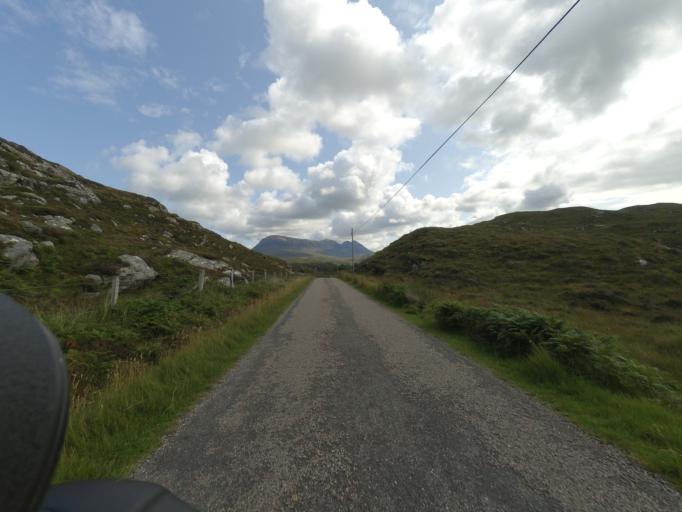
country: GB
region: Scotland
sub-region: Highland
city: Ullapool
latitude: 58.2423
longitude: -5.1860
